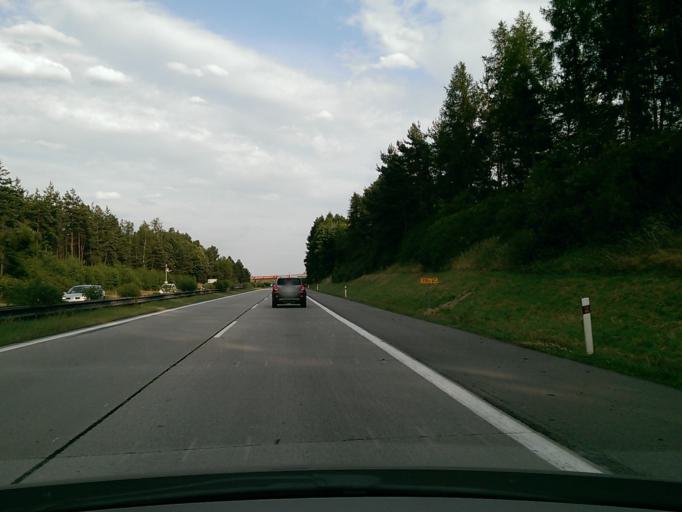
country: CZ
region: Vysocina
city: Velky Beranov
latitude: 49.4369
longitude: 15.6424
